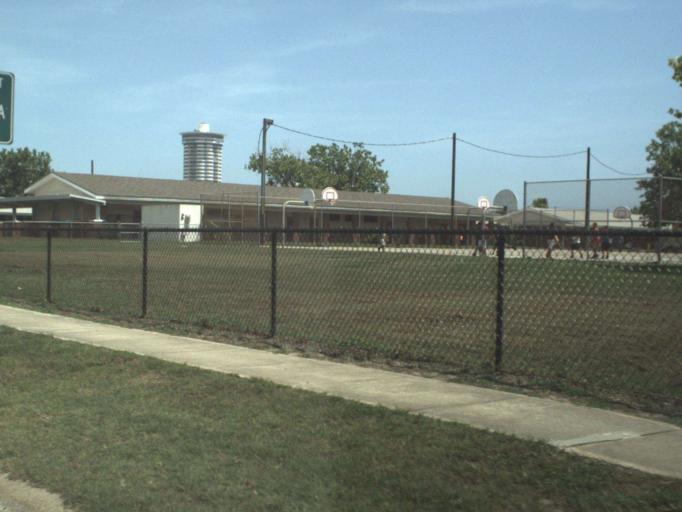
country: US
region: Florida
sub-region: Volusia County
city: Daytona Beach Shores
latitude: 29.1756
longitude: -80.9863
